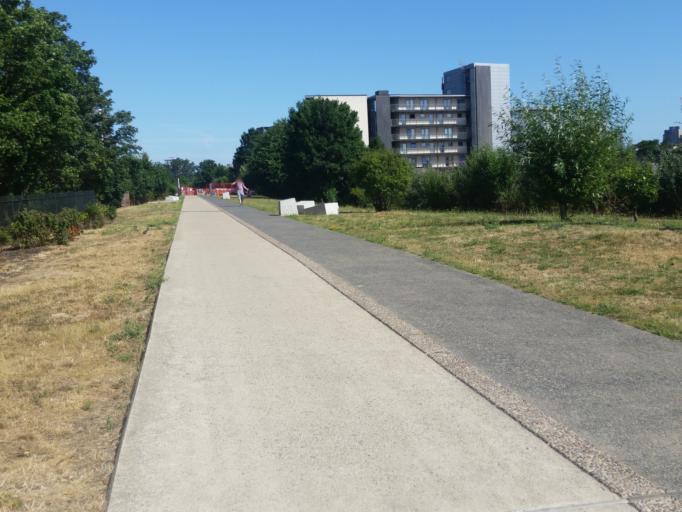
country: GB
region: England
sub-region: Greater London
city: Poplar
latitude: 51.5374
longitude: -0.0239
